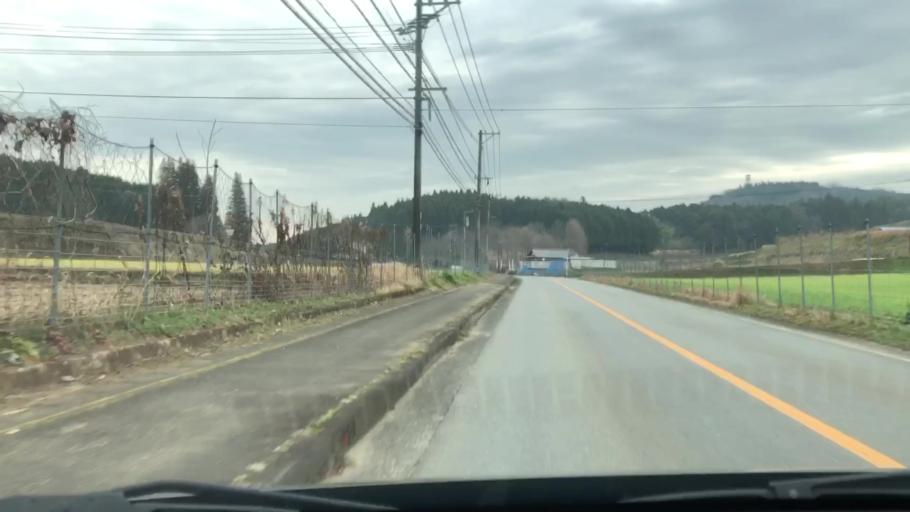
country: JP
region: Oita
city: Usuki
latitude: 33.0048
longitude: 131.6532
